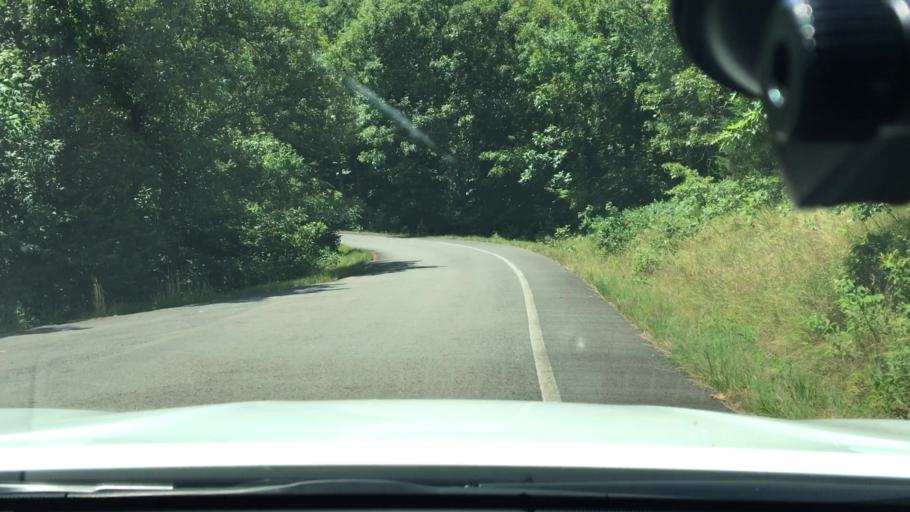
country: US
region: Arkansas
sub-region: Logan County
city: Paris
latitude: 35.1724
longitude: -93.6406
